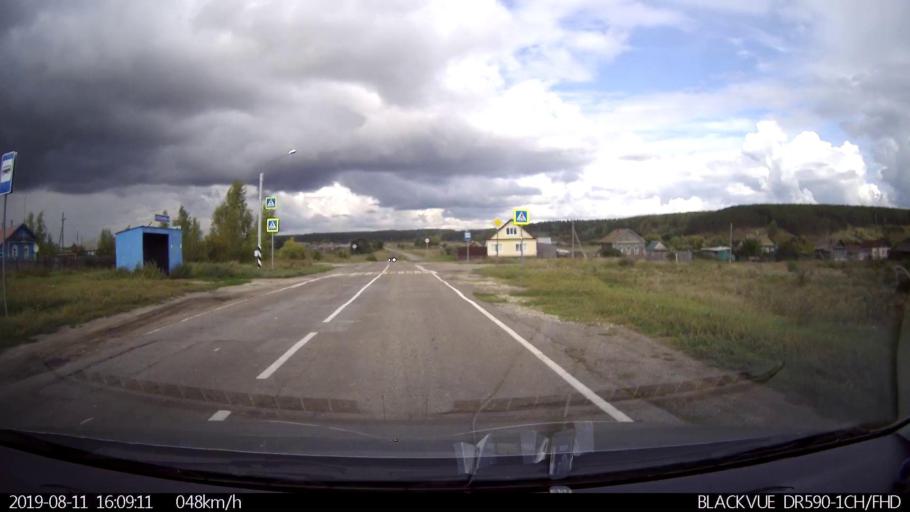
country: RU
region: Ulyanovsk
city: Ignatovka
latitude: 53.9903
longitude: 47.6509
